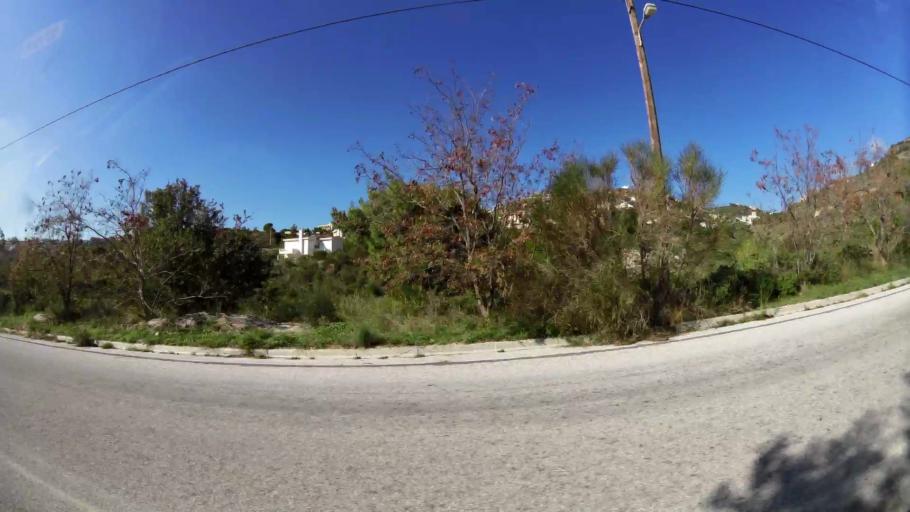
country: GR
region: Attica
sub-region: Nomarchia Anatolikis Attikis
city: Dhrafi
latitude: 38.0384
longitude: 23.9049
